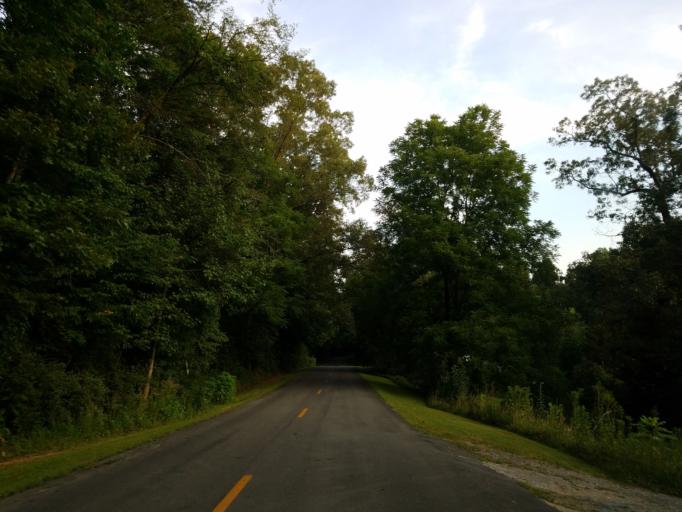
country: US
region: Georgia
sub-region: Pickens County
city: Nelson
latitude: 34.3910
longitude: -84.3746
